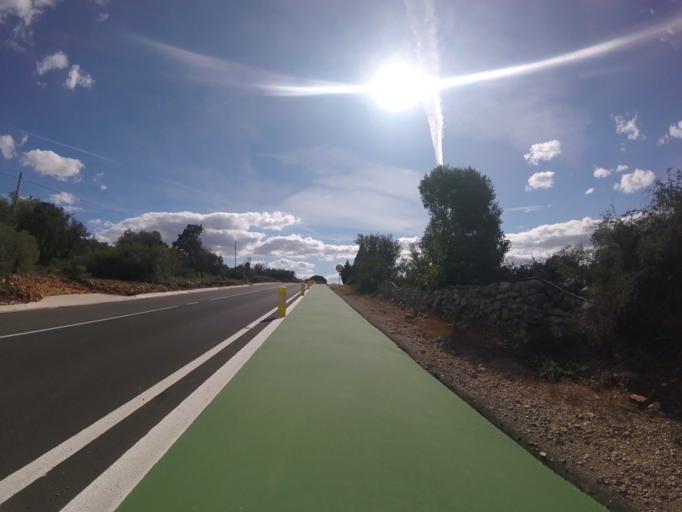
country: ES
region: Valencia
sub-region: Provincia de Castello
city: Albocasser
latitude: 40.4107
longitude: 0.0713
